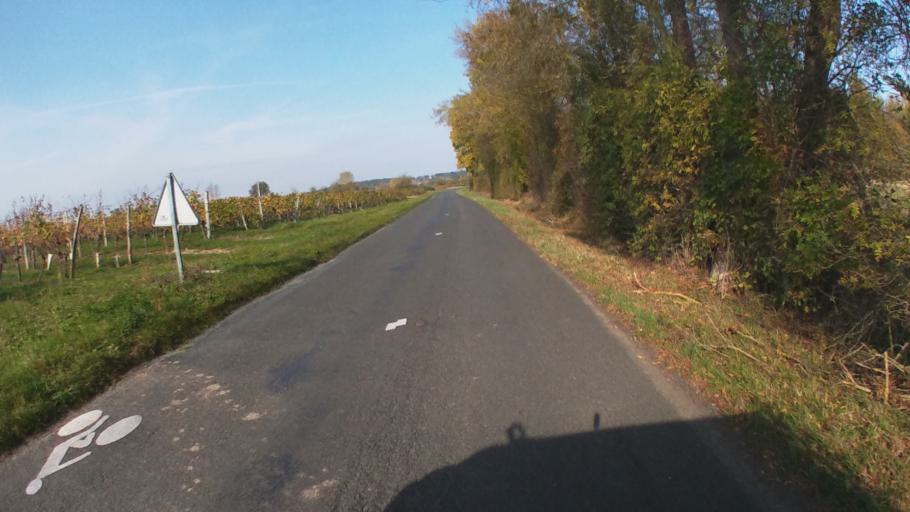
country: FR
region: Pays de la Loire
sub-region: Departement de Maine-et-Loire
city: Chace
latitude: 47.2104
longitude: -0.0897
